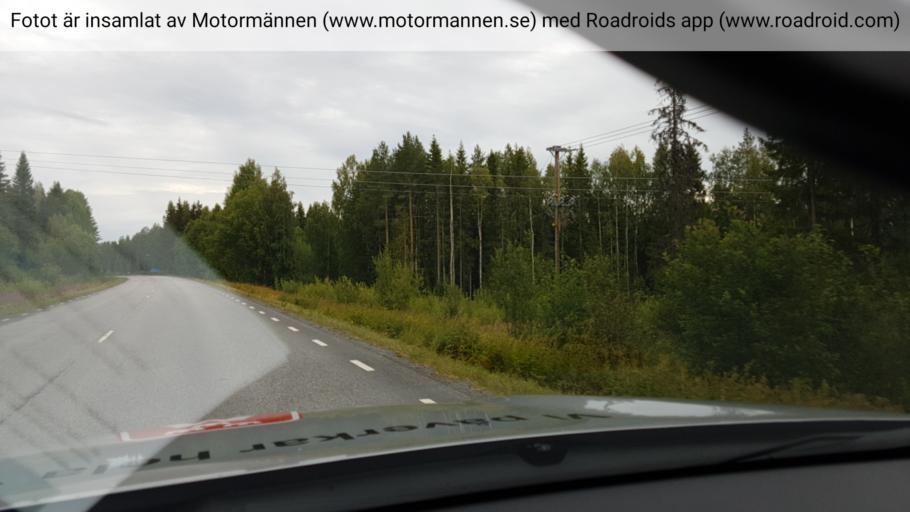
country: SE
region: Norrbotten
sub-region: Bodens Kommun
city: Boden
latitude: 65.8050
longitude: 21.6568
